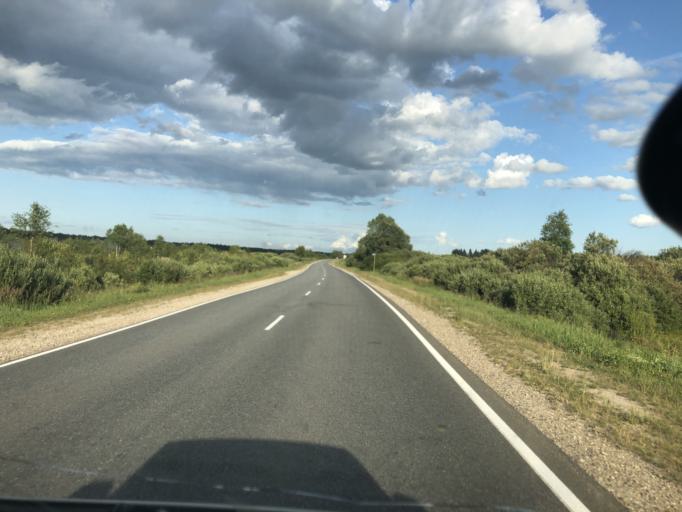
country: RU
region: Kaluga
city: Yukhnov
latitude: 54.7000
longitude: 35.2762
